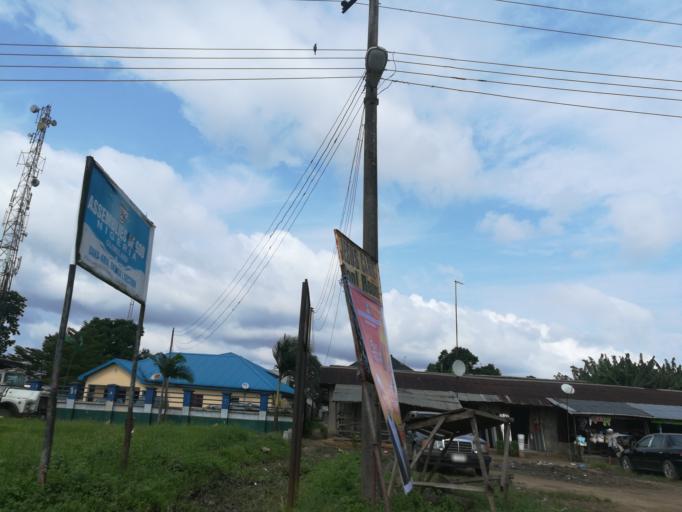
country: NG
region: Rivers
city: Okrika
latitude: 4.7492
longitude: 7.0997
